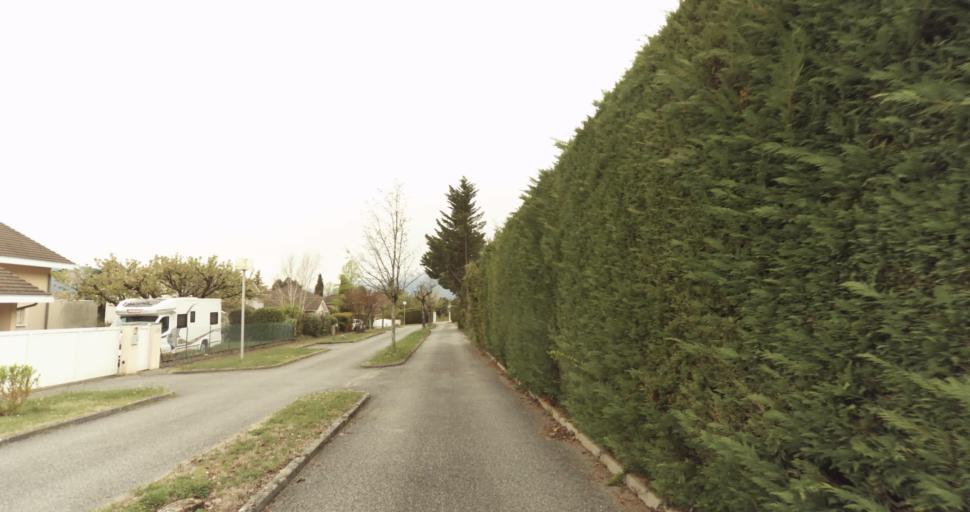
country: FR
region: Rhone-Alpes
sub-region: Departement de l'Isere
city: Biviers
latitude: 45.2347
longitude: 5.8140
